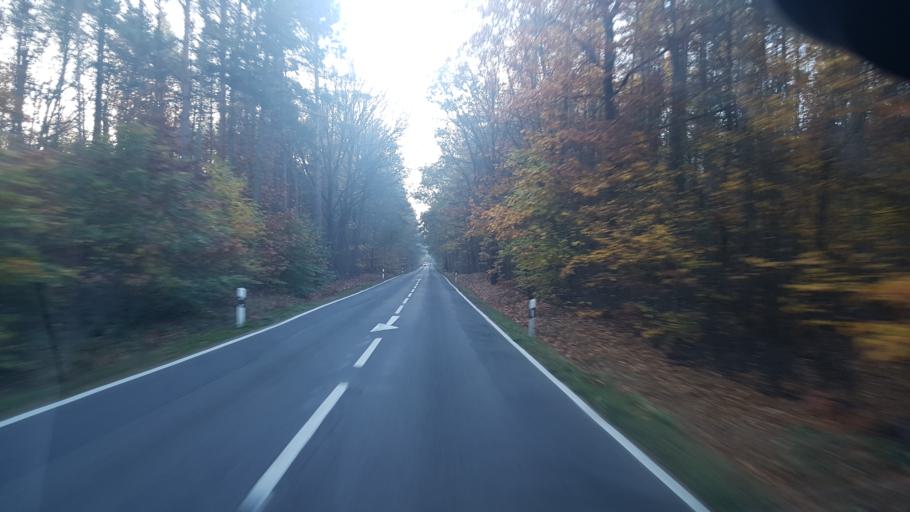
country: DE
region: Saxony
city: Dahlen
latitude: 51.4148
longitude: 12.9719
